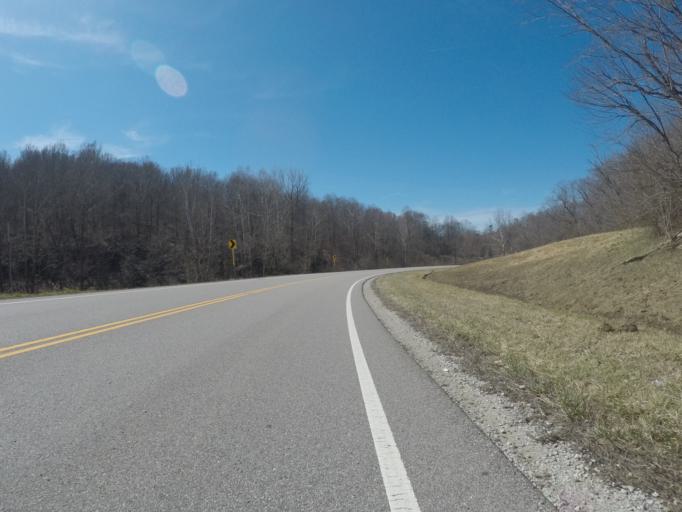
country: US
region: Ohio
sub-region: Lawrence County
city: South Point
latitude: 38.4853
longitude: -82.5613
